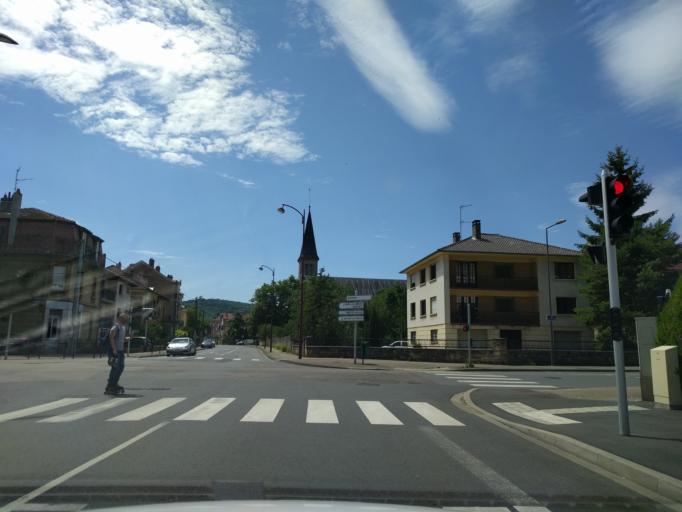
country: FR
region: Lorraine
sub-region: Departement de la Moselle
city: Le Ban Saint-Martin
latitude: 49.1347
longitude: 6.1574
